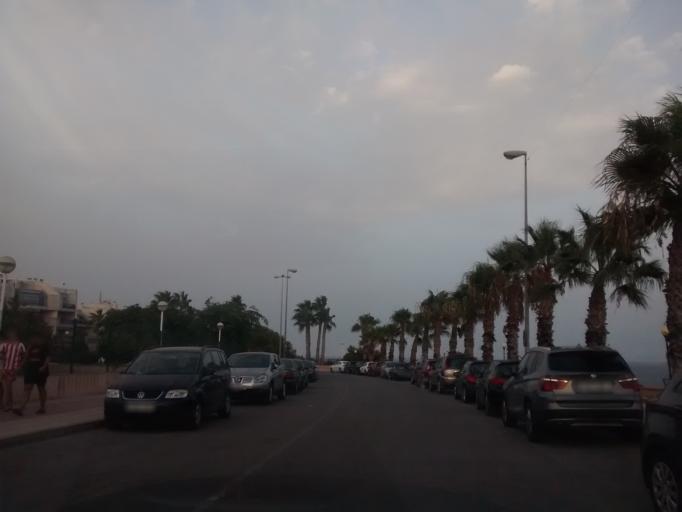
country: ES
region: Valencia
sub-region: Provincia de Alicante
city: Pilar de la Horadada
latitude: 37.9099
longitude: -0.7393
